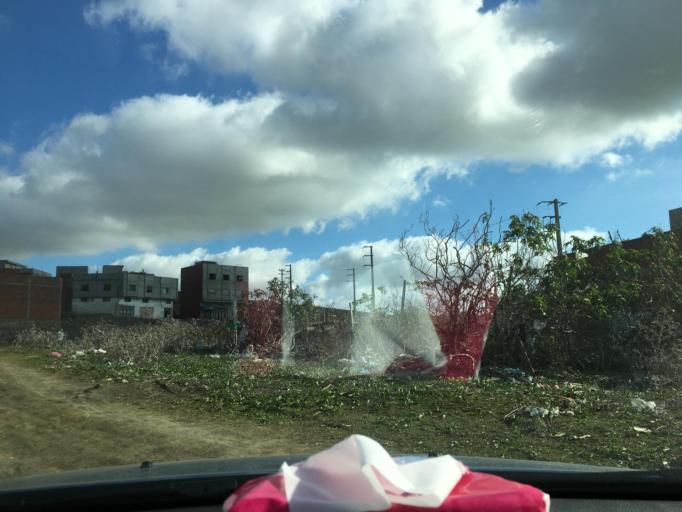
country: MA
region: Tanger-Tetouan
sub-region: Tanger-Assilah
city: Tangier
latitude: 35.7146
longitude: -5.8161
